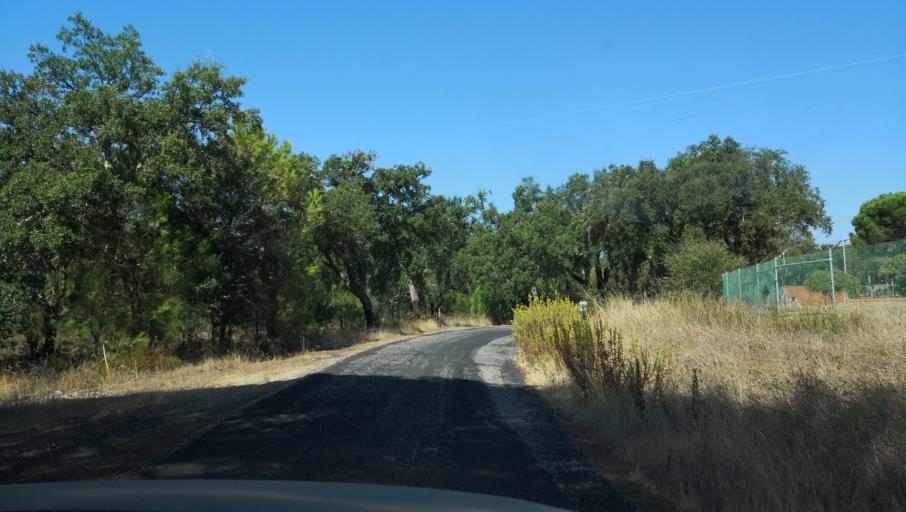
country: PT
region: Setubal
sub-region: Alcacer do Sal
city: Alcacer do Sal
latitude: 38.2662
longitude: -8.3158
